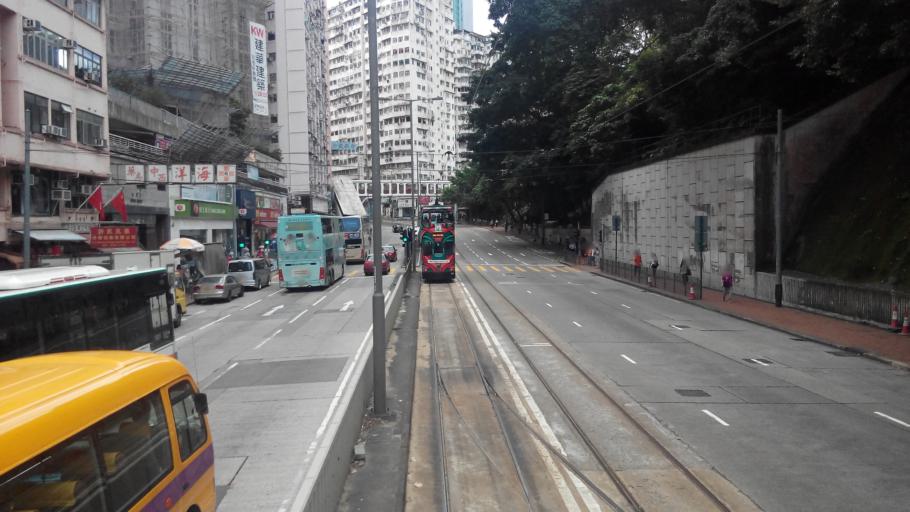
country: HK
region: Wanchai
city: Wan Chai
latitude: 22.2863
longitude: 114.2107
